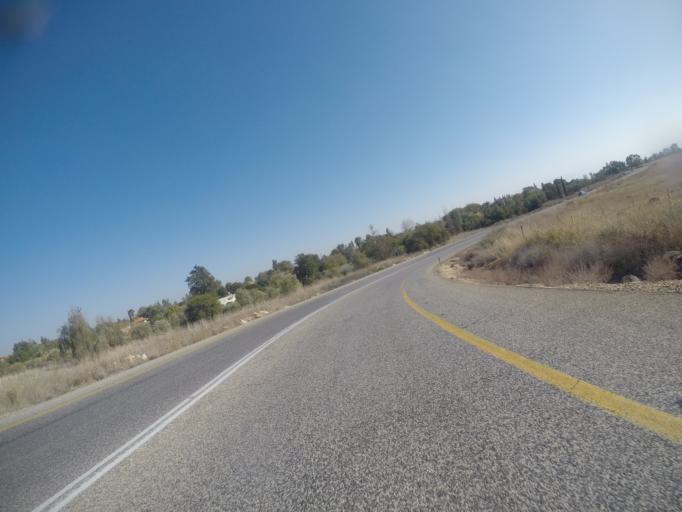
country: IL
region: Northern District
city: Rosh Pinna
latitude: 32.9096
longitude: 35.5490
